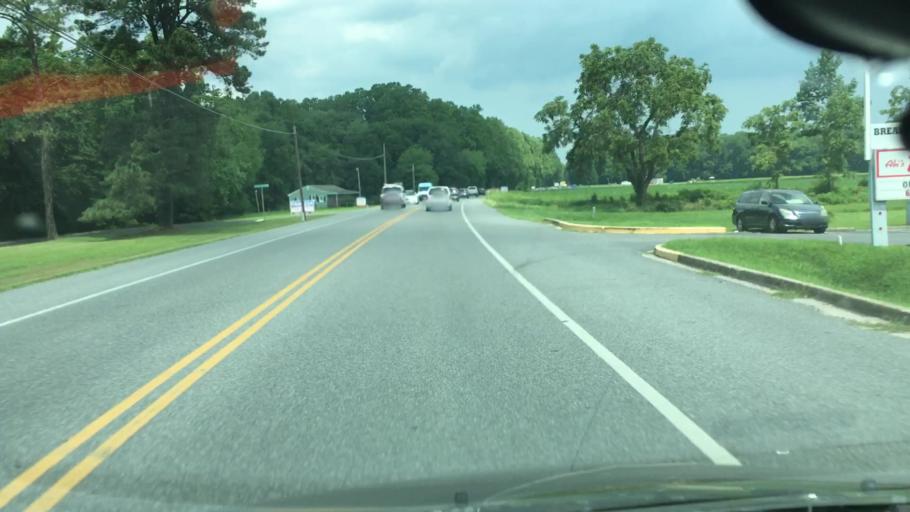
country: US
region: Maryland
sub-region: Worcester County
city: Ocean Pines
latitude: 38.3612
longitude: -75.1685
